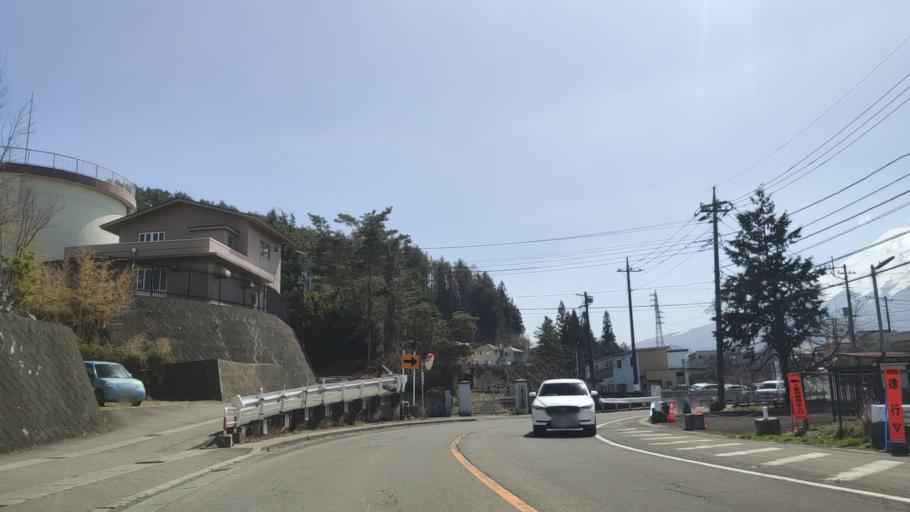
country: JP
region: Yamanashi
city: Fujikawaguchiko
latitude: 35.4761
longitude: 138.8155
